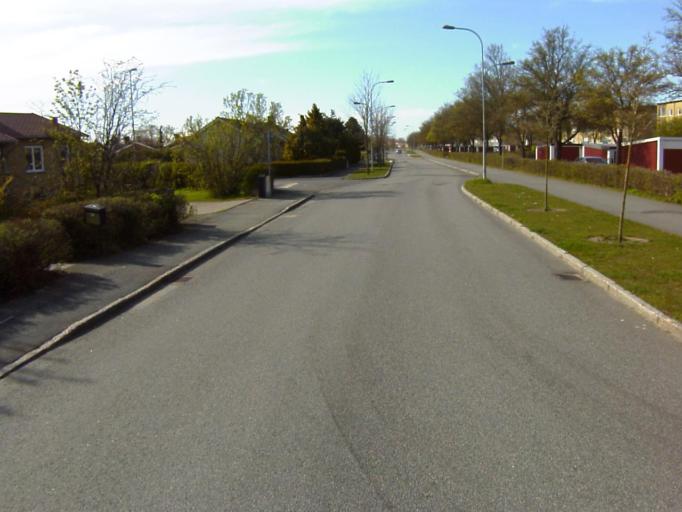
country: SE
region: Skane
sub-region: Kristianstads Kommun
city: Kristianstad
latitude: 56.0554
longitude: 14.1566
